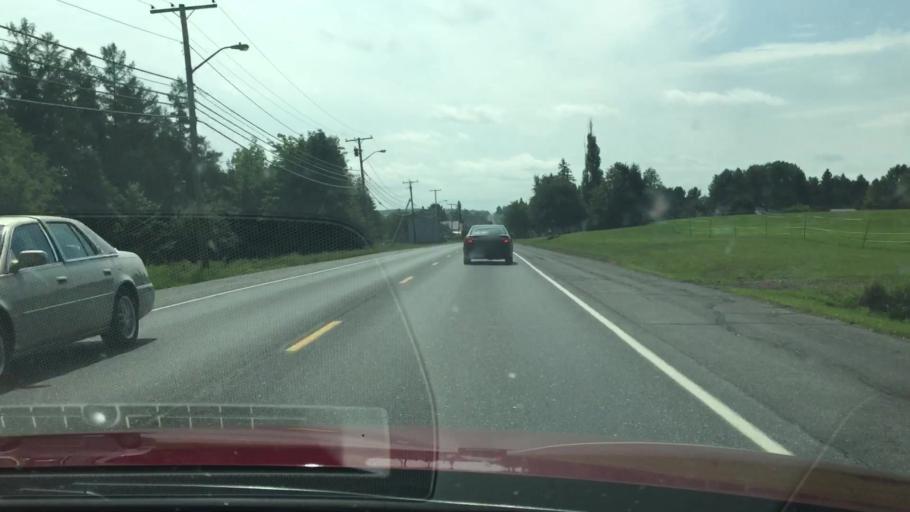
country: US
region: Maine
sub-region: Aroostook County
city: Easton
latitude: 46.4318
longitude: -67.8438
